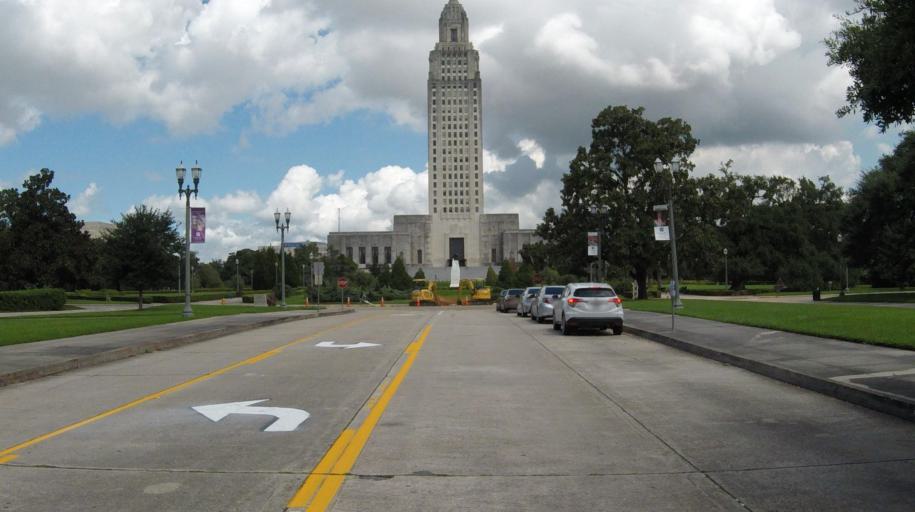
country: US
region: Louisiana
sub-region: West Baton Rouge Parish
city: Port Allen
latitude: 30.4540
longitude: -91.1873
